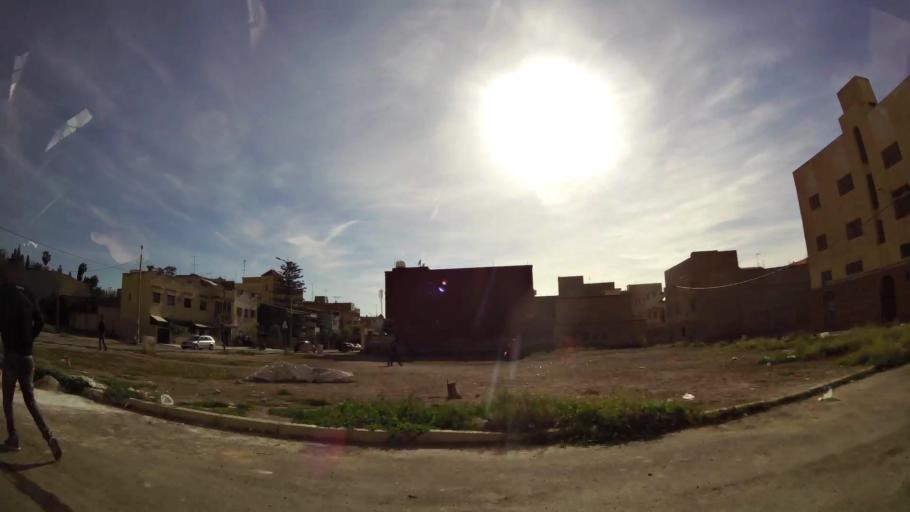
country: MA
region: Oriental
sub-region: Oujda-Angad
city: Oujda
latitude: 34.6753
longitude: -1.9058
